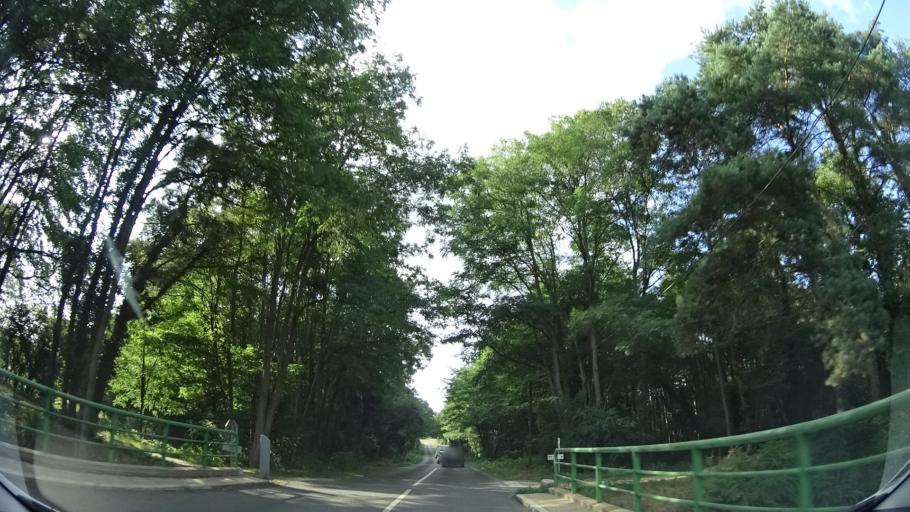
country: FR
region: Pays de la Loire
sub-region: Departement de la Loire-Atlantique
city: Casson
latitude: 47.4039
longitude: -1.5322
